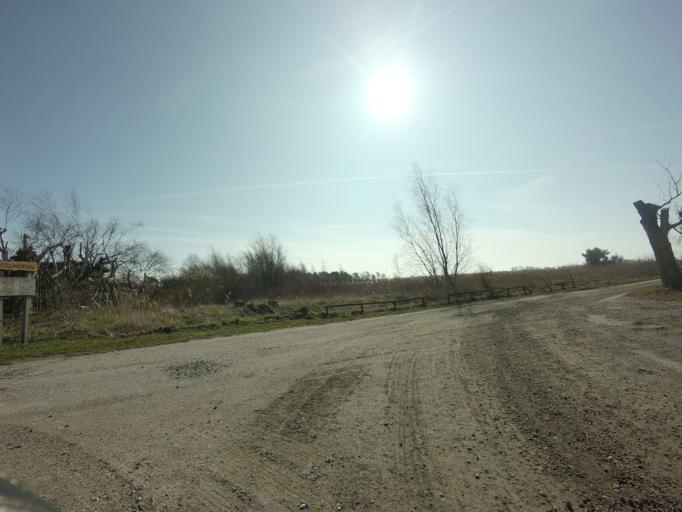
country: SE
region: Skane
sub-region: Vellinge Kommun
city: Skanor med Falsterbo
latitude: 55.4332
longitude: 12.8580
